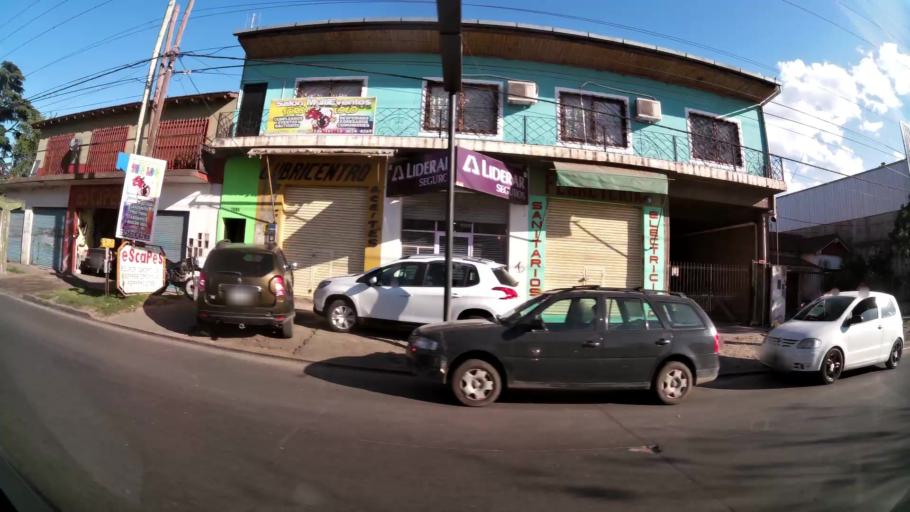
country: AR
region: Buenos Aires
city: Hurlingham
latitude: -34.5048
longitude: -58.7187
